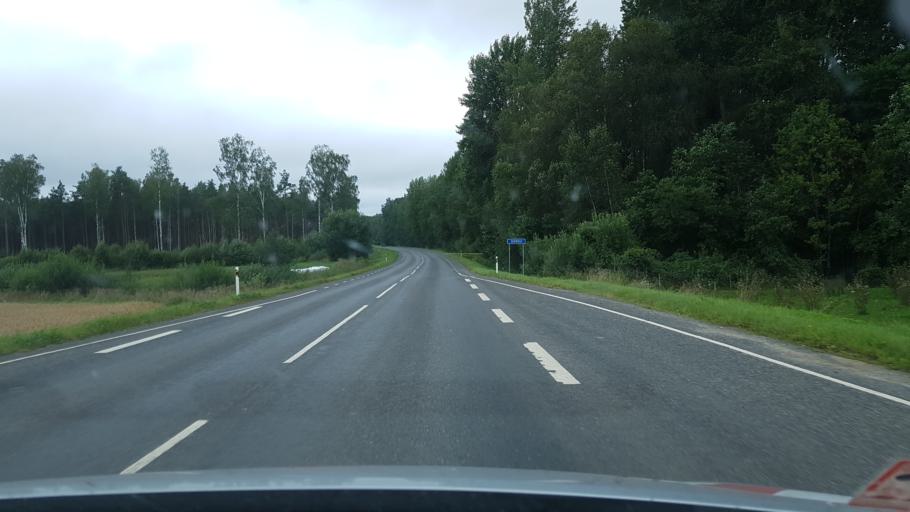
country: EE
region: Jogevamaa
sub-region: Poltsamaa linn
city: Poltsamaa
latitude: 58.5287
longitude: 25.8769
